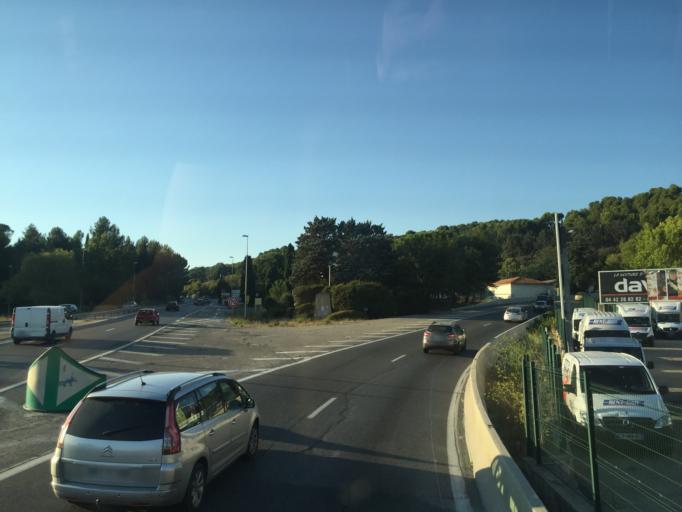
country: FR
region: Provence-Alpes-Cote d'Azur
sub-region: Departement des Bouches-du-Rhone
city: Aix-en-Provence
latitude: 43.5483
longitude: 5.4280
